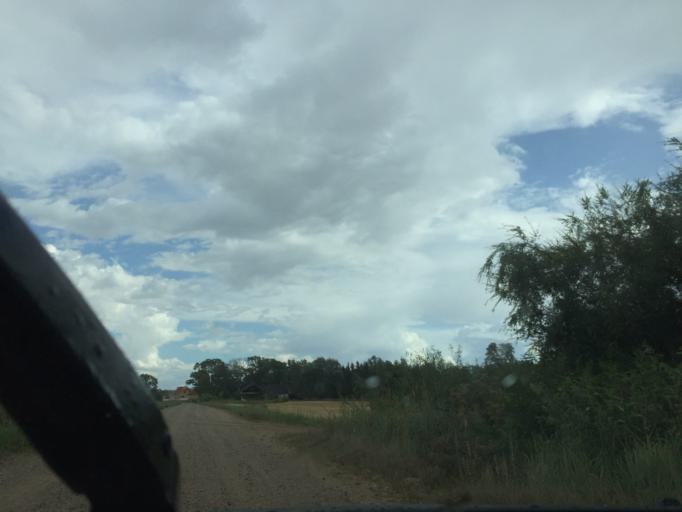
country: LT
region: Siauliu apskritis
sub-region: Joniskis
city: Joniskis
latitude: 56.3475
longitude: 23.5431
